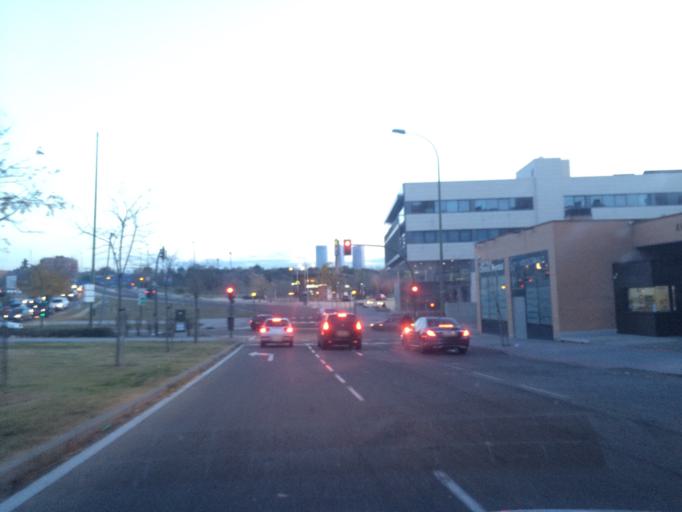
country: ES
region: Madrid
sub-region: Provincia de Madrid
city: Las Tablas
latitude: 40.5030
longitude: -3.6981
